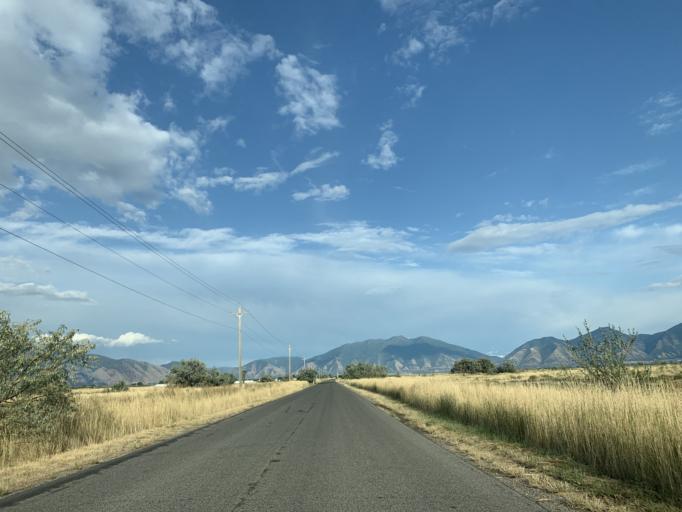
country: US
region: Utah
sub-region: Utah County
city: West Mountain
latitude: 40.1142
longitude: -111.7954
